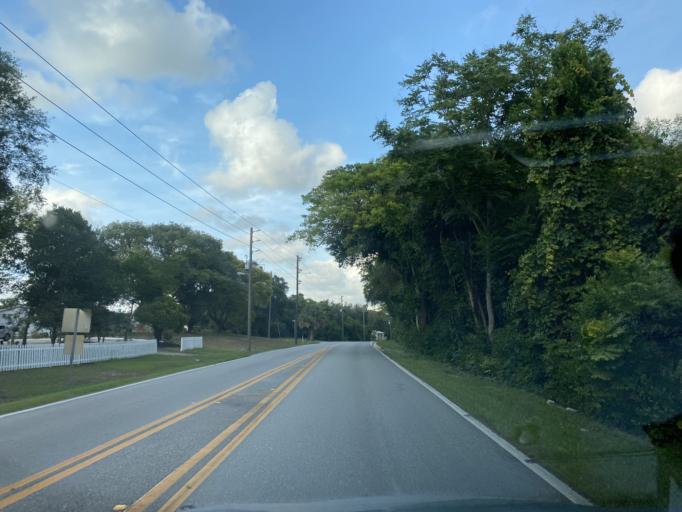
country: US
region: Florida
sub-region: Volusia County
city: DeBary
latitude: 28.8680
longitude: -81.3096
